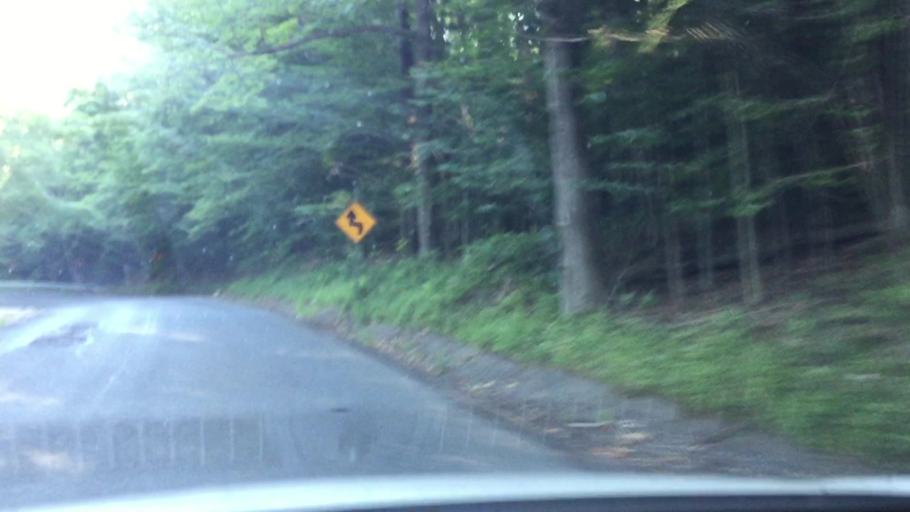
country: US
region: Massachusetts
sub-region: Berkshire County
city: Becket
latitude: 42.2974
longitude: -73.1522
